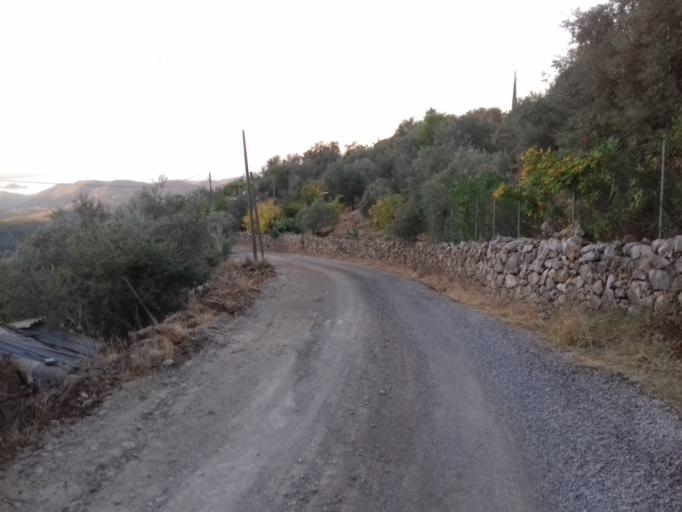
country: TR
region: Mugla
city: Yaniklar
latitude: 36.7862
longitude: 29.0203
